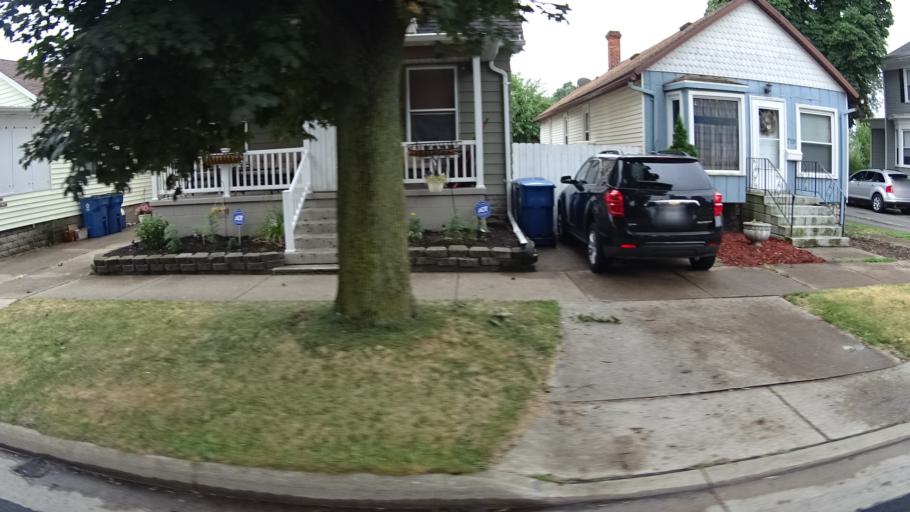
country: US
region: Ohio
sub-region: Erie County
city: Sandusky
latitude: 41.4493
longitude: -82.7091
